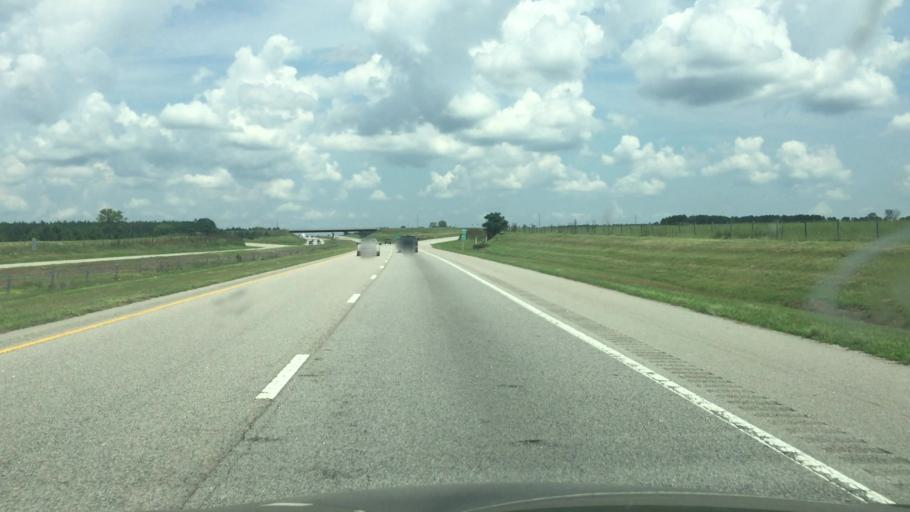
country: US
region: North Carolina
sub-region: Richmond County
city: Ellerbe
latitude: 35.1405
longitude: -79.7137
